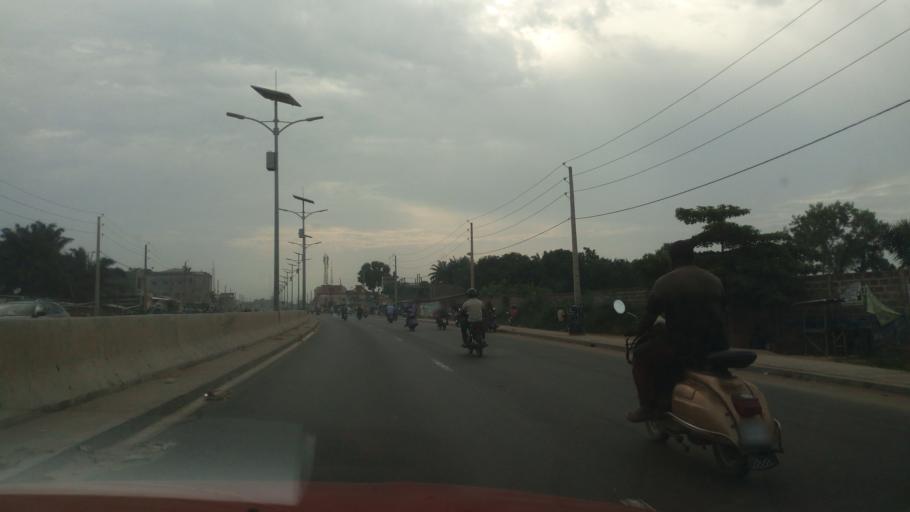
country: BJ
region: Atlantique
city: Hevie
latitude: 6.3866
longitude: 2.2935
